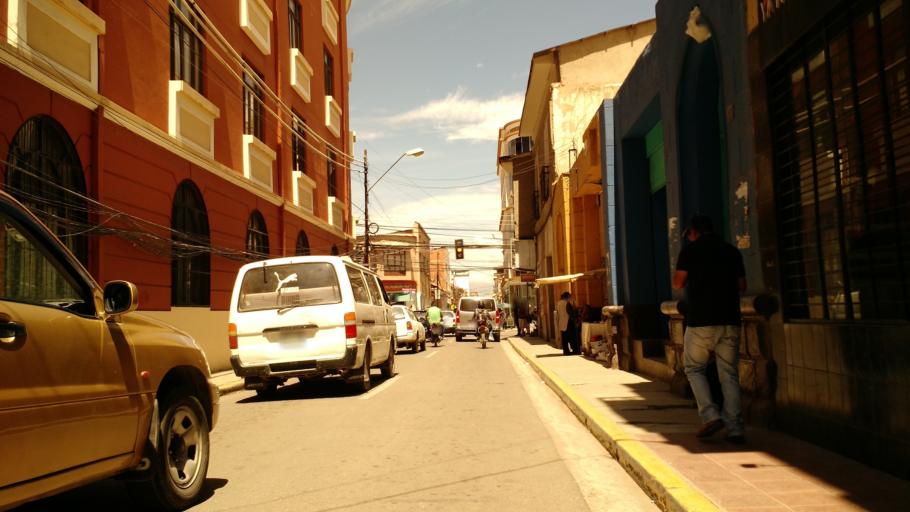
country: BO
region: Cochabamba
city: Cochabamba
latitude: -17.3956
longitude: -66.1578
